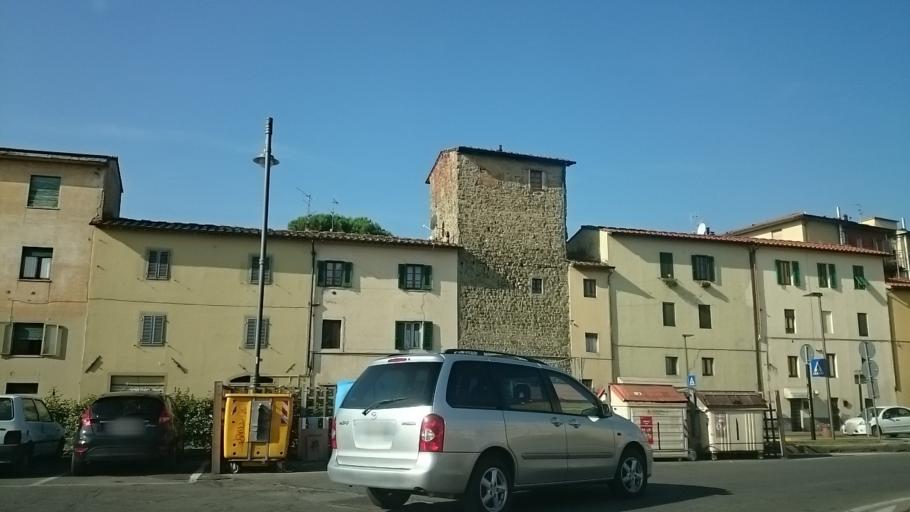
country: IT
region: Tuscany
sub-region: Province of Florence
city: Figline Valdarno
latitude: 43.6187
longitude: 11.4747
